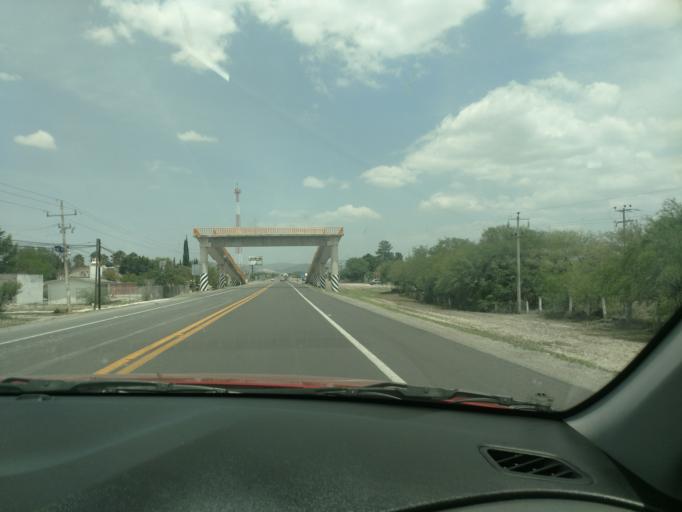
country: MX
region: San Luis Potosi
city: Rio Verde
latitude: 21.9188
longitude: -99.9528
